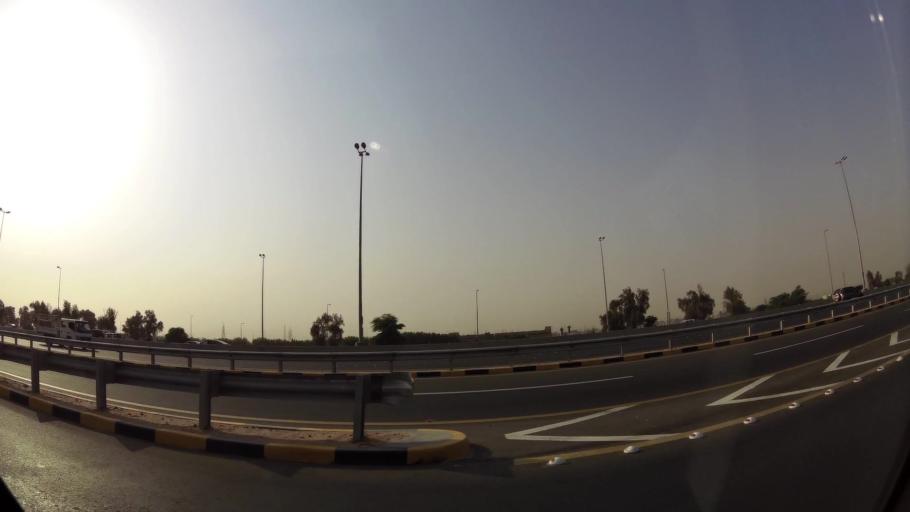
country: KW
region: Al Asimah
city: Ar Rabiyah
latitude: 29.3116
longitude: 47.8150
